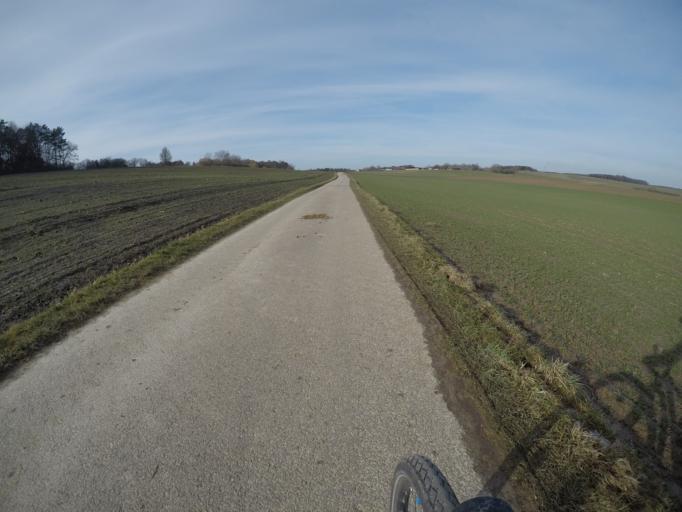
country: DE
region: Baden-Wuerttemberg
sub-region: Karlsruhe Region
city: Ostelsheim
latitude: 48.6984
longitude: 8.8669
